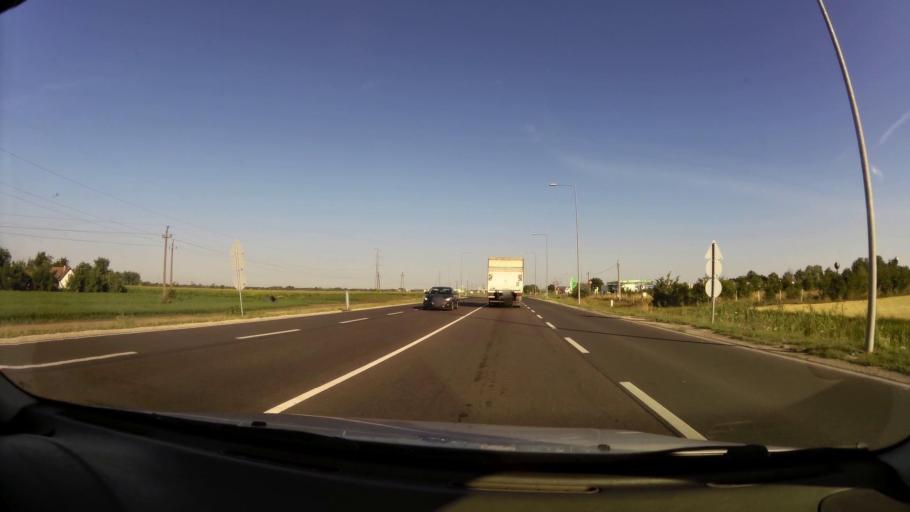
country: HU
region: Pest
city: Cegled
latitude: 47.2025
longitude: 19.7819
